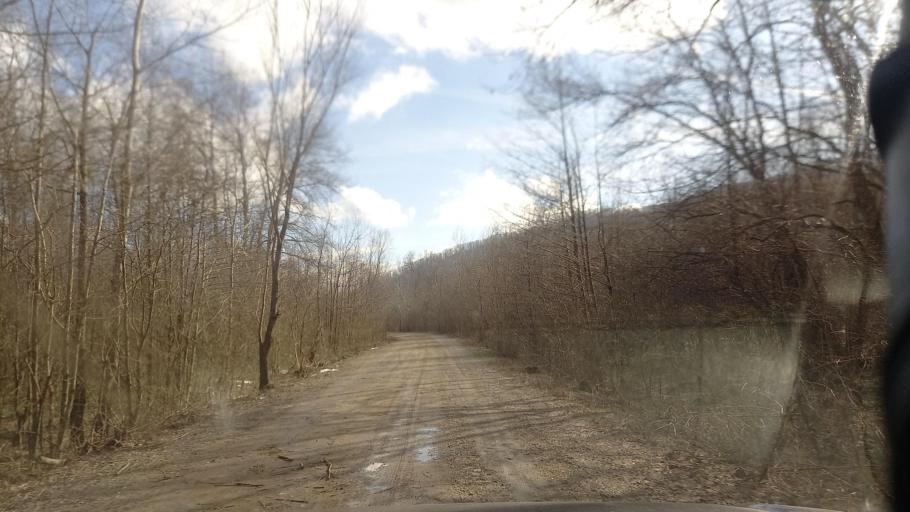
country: RU
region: Krasnodarskiy
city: Smolenskaya
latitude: 44.6191
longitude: 38.8262
